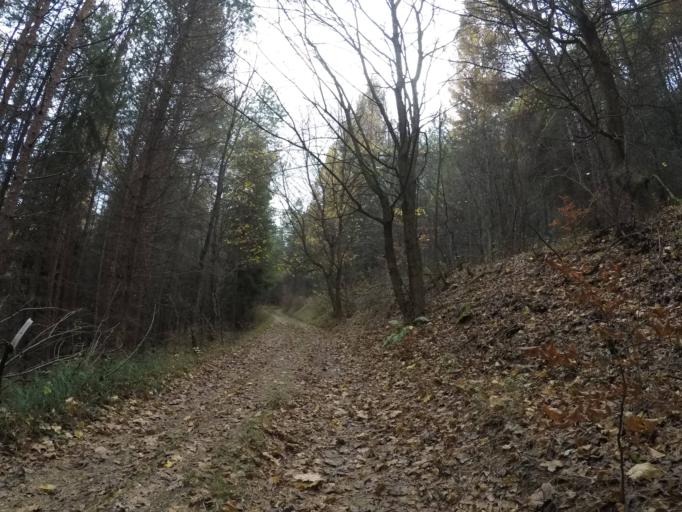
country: SK
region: Presovsky
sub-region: Okres Presov
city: Presov
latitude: 48.9004
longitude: 21.1678
